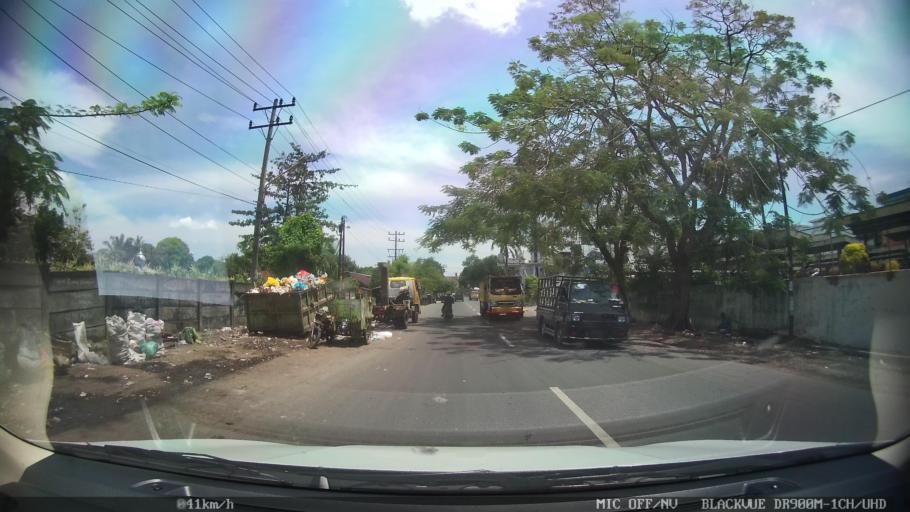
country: ID
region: North Sumatra
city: Binjai
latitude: 3.6063
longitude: 98.4950
